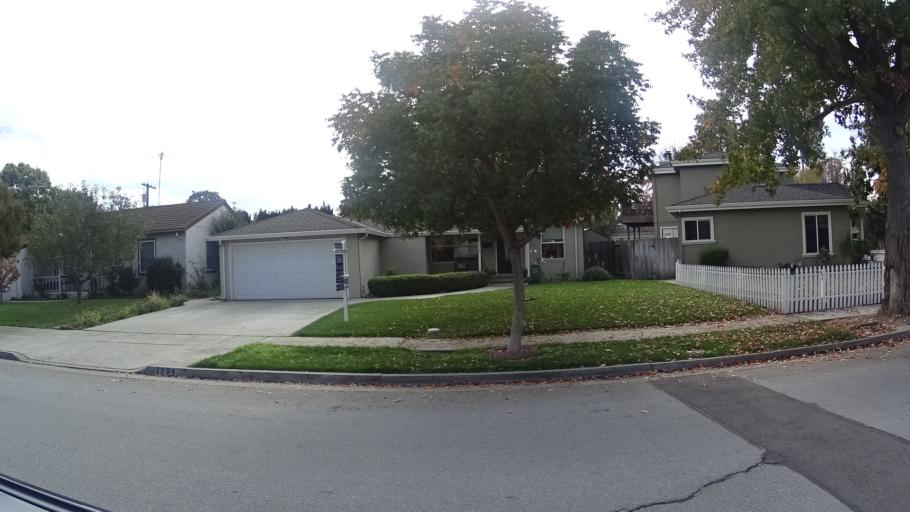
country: US
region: California
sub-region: Santa Clara County
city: Burbank
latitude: 37.3349
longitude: -121.9432
